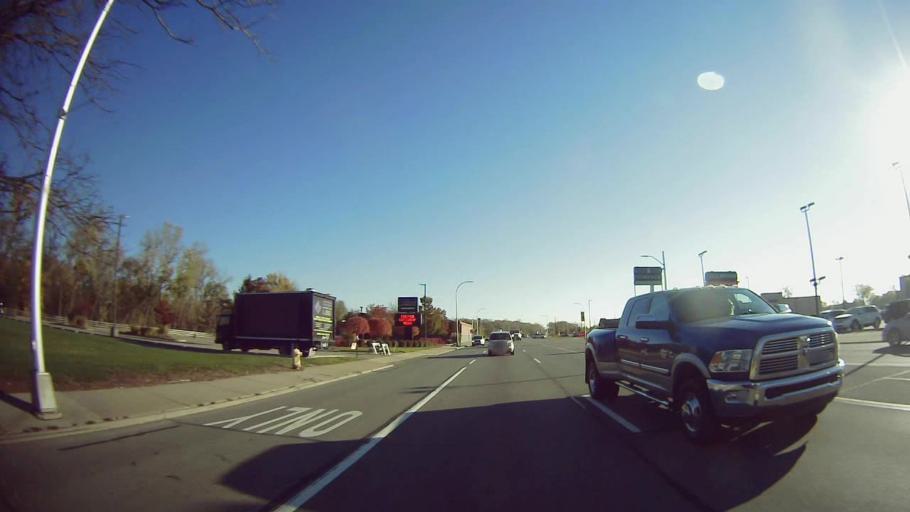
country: US
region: Michigan
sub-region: Wayne County
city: Dearborn Heights
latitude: 42.3075
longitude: -83.2387
